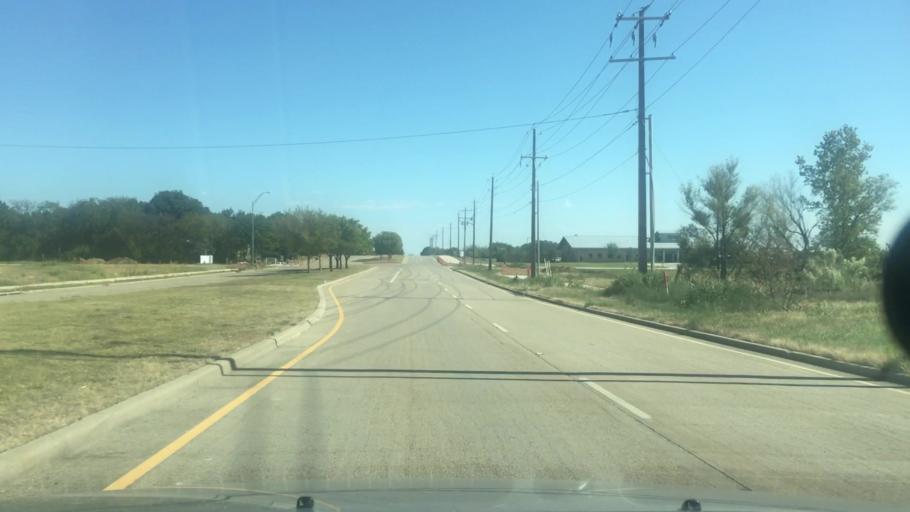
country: US
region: Texas
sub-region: Denton County
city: Denton
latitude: 33.2490
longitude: -97.1494
